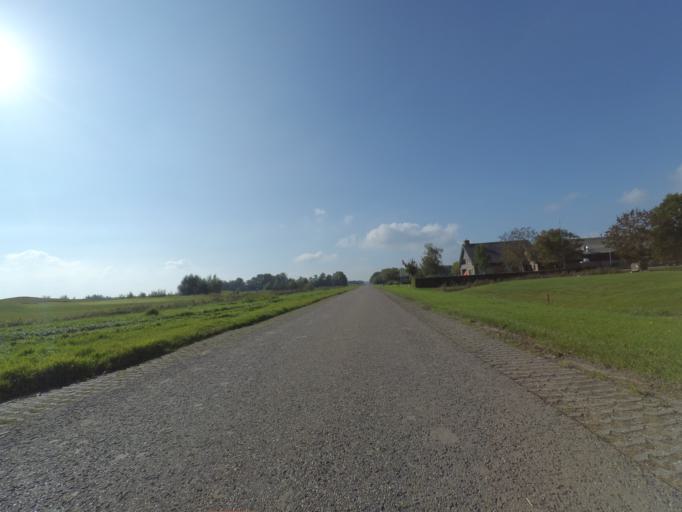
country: NL
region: Flevoland
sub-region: Gemeente Dronten
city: Biddinghuizen
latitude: 52.4125
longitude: 5.6876
